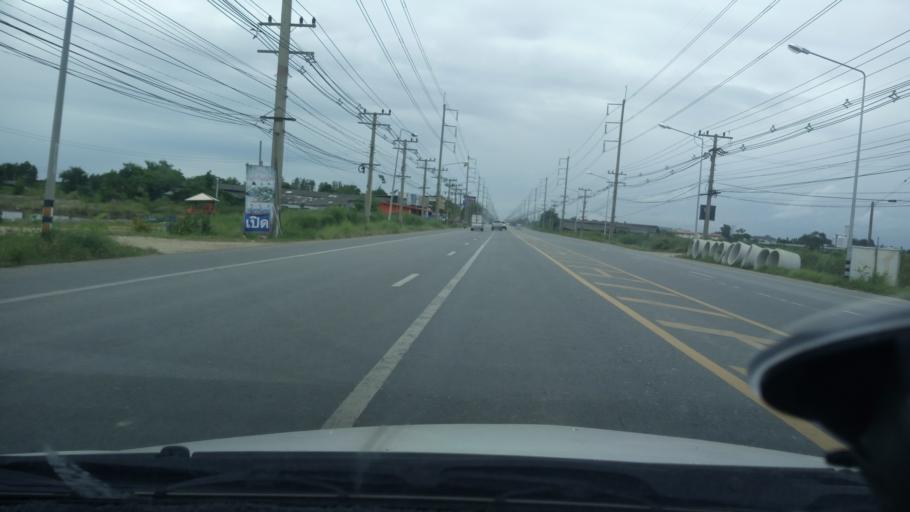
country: TH
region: Chon Buri
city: Phanat Nikhom
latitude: 13.4759
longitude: 101.1694
